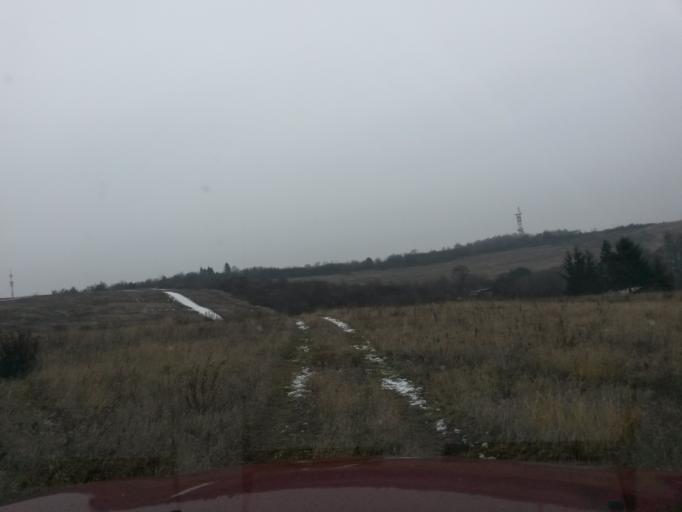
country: SK
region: Kosicky
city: Kosice
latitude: 48.7181
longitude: 21.2843
